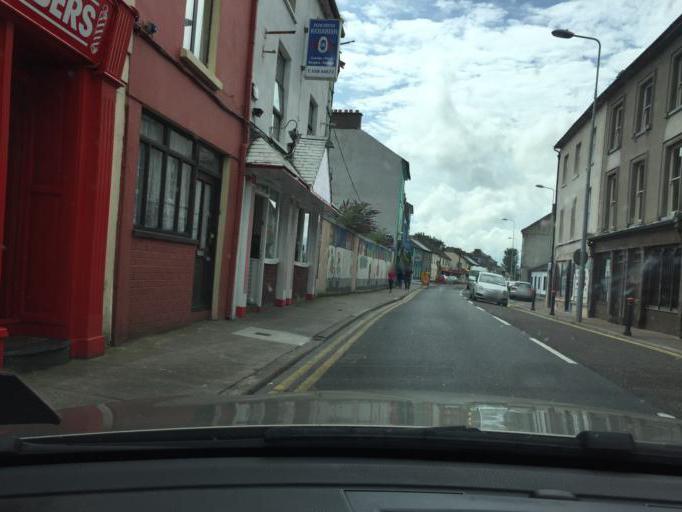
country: IE
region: Munster
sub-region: Waterford
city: Dungarvan
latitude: 52.0894
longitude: -7.6229
